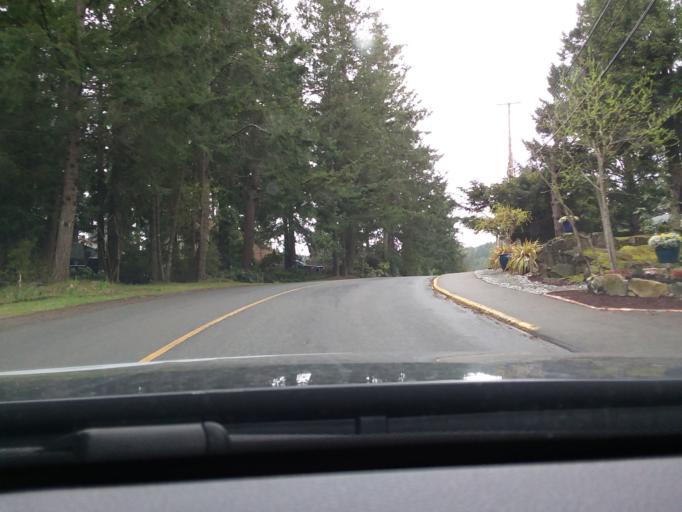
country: CA
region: British Columbia
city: North Saanich
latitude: 48.6176
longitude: -123.4259
